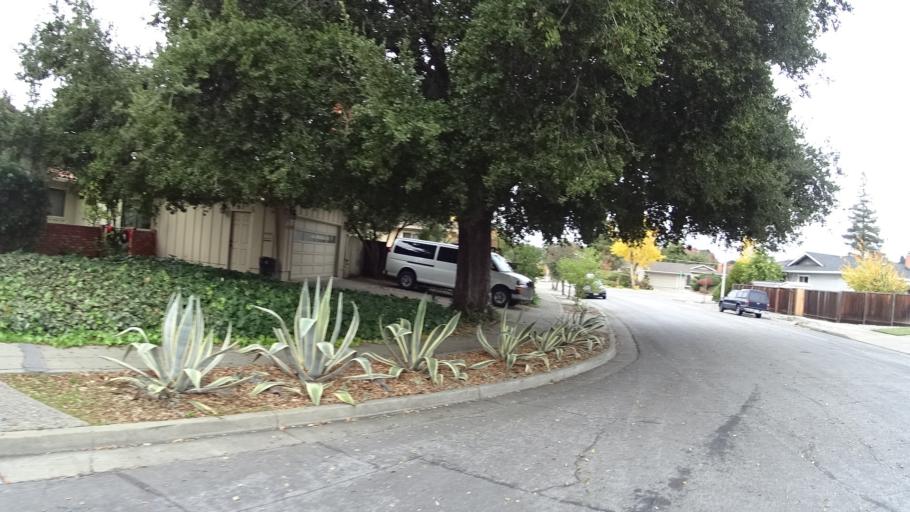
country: US
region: California
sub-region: Santa Clara County
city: Sunnyvale
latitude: 37.3581
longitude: -122.0446
